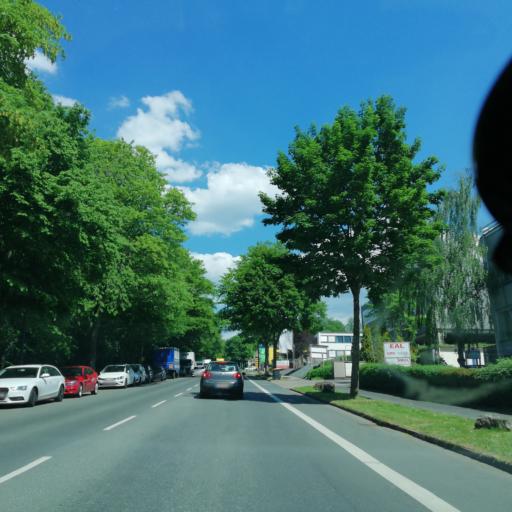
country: DE
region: North Rhine-Westphalia
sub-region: Regierungsbezirk Dusseldorf
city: Wuppertal
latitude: 51.2584
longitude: 7.1099
